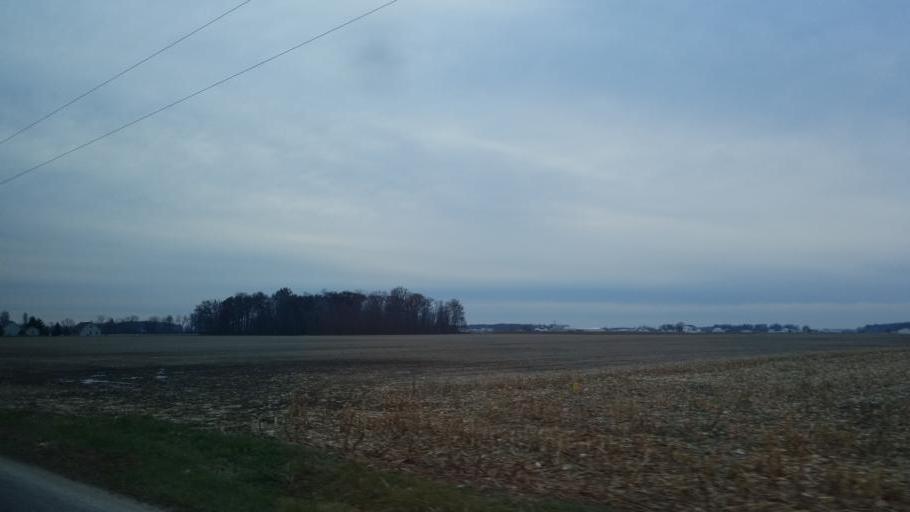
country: US
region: Indiana
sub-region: Adams County
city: Berne
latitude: 40.7272
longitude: -84.8796
